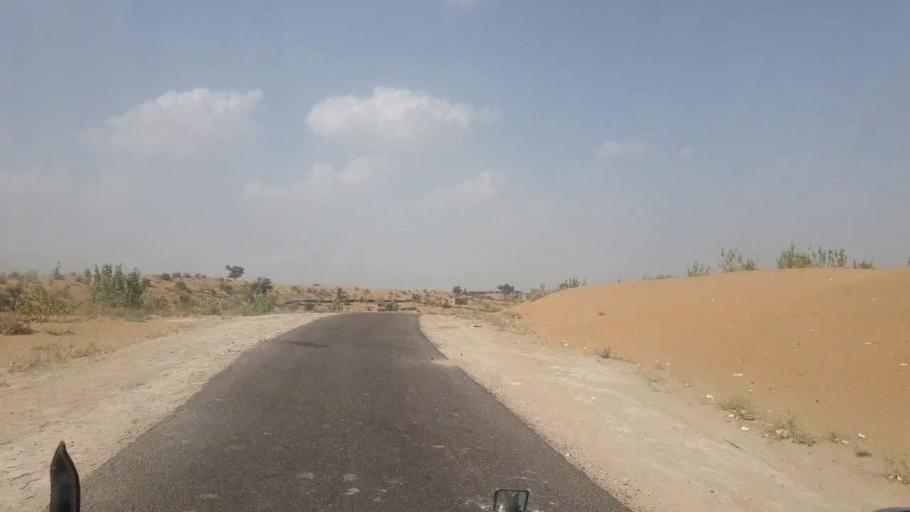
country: PK
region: Sindh
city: Islamkot
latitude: 25.2107
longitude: 70.2833
